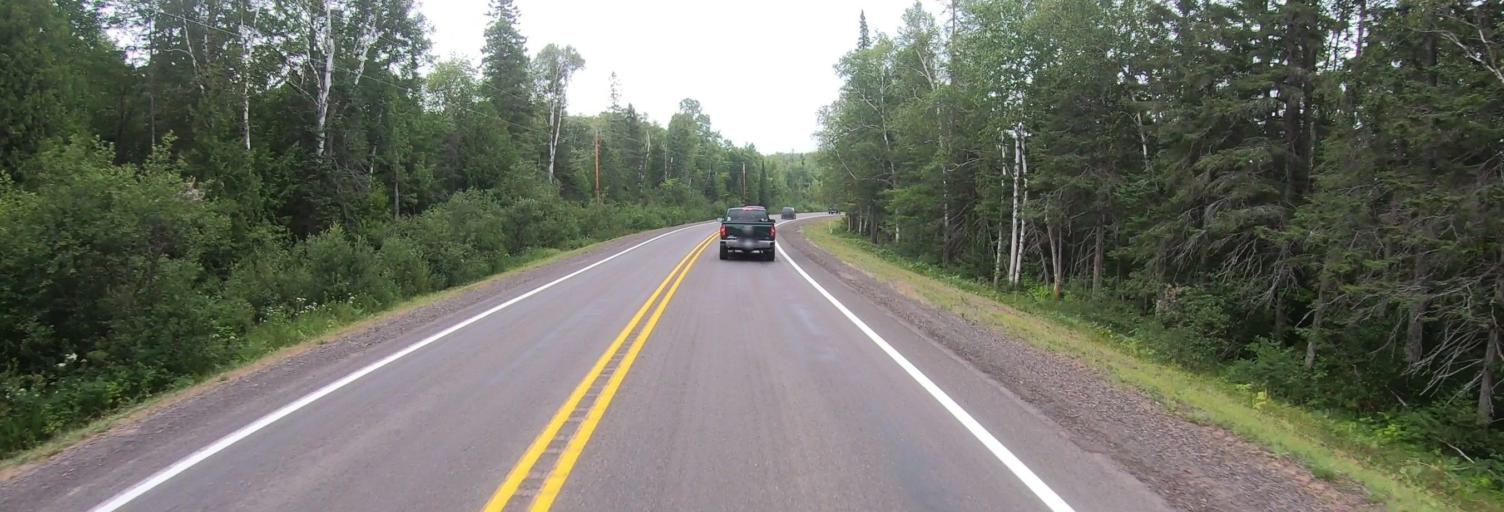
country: US
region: Michigan
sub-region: Keweenaw County
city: Eagle River
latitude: 47.4173
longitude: -88.1367
